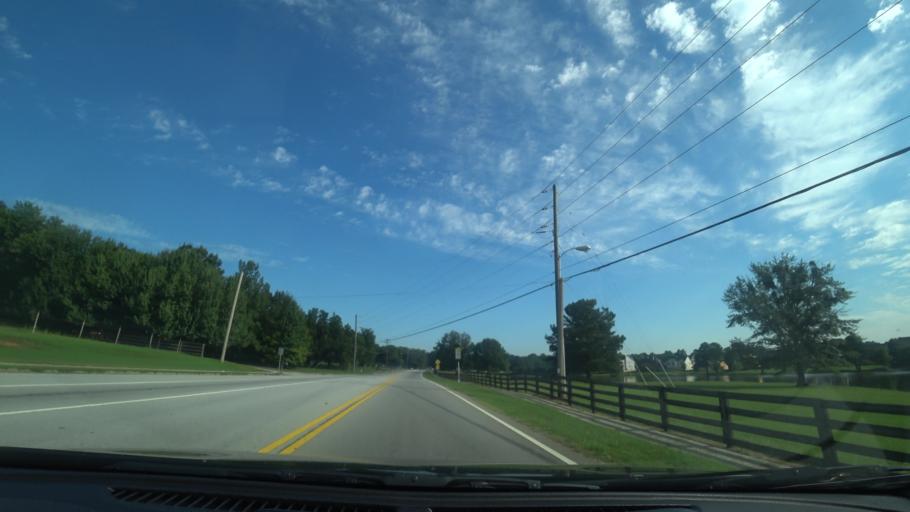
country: US
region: Georgia
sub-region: Gwinnett County
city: Grayson
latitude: 33.8737
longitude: -83.9562
